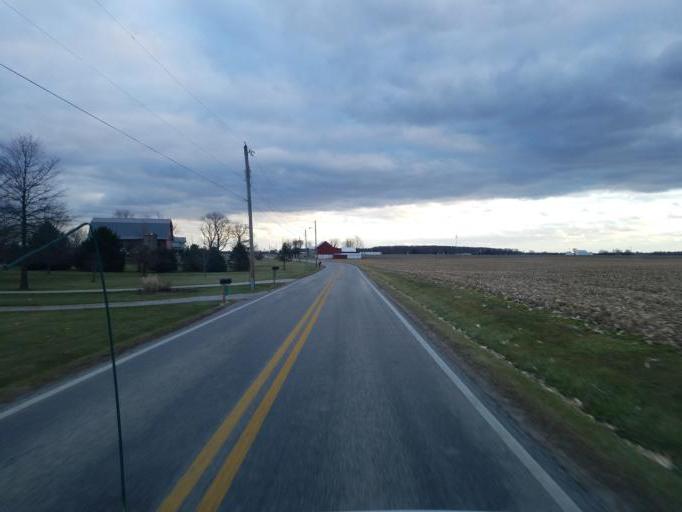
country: US
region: Ohio
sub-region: Delaware County
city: Delaware
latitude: 40.3343
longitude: -83.1133
